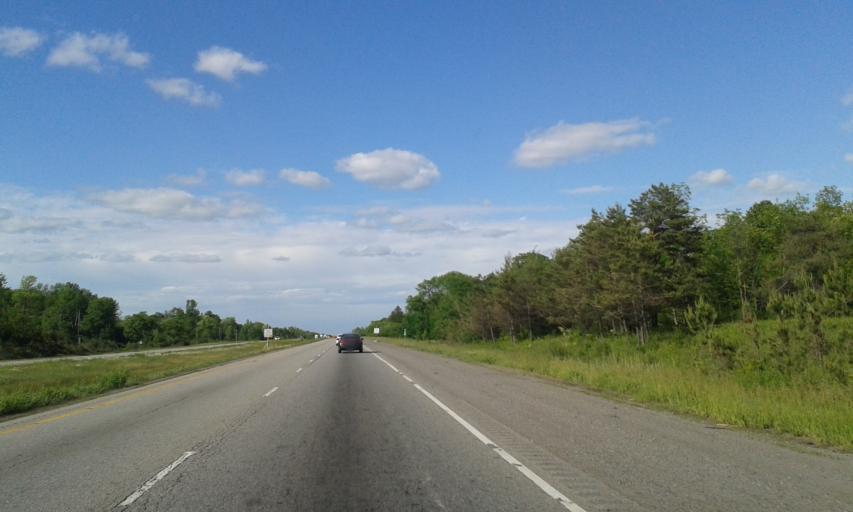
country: CA
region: Ontario
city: Prescott
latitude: 44.6742
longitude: -75.6004
